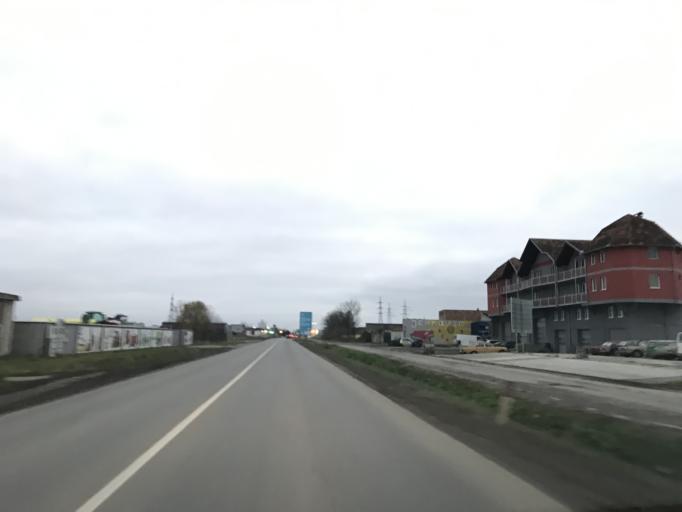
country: RS
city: Rumenka
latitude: 45.2832
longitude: 19.7708
